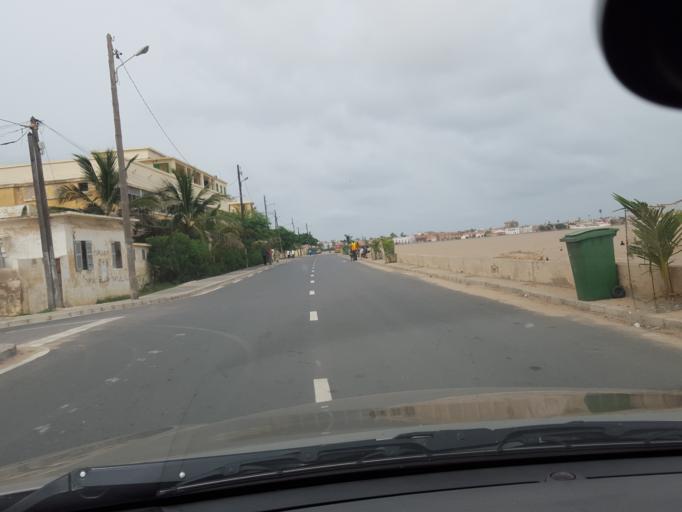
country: SN
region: Saint-Louis
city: Saint-Louis
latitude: 16.0306
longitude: -16.4941
